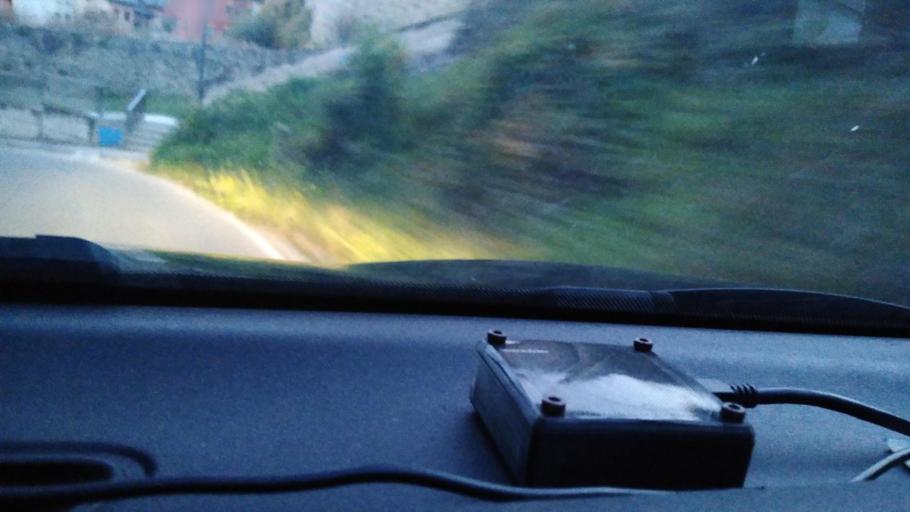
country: ES
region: Catalonia
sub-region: Provincia de Girona
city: Puigcerda
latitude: 42.4343
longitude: 1.9303
